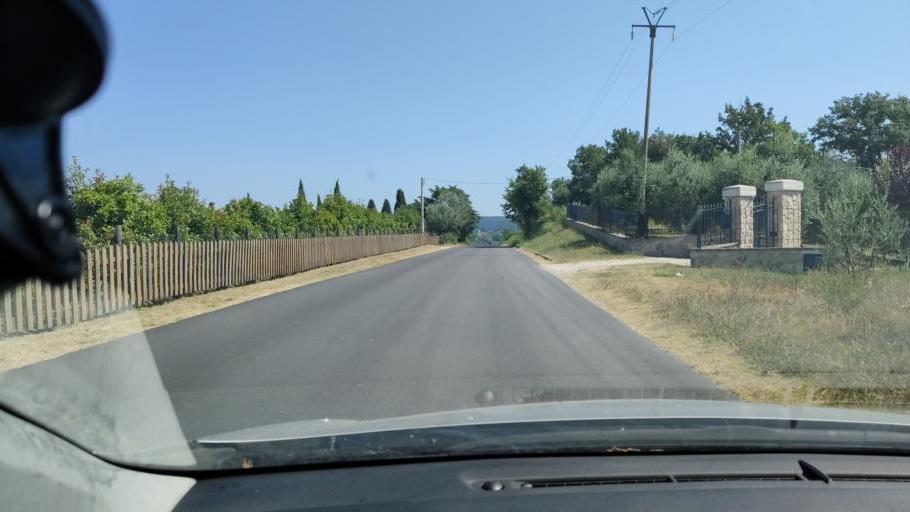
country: IT
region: Umbria
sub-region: Provincia di Terni
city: Fornole
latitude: 42.5212
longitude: 12.4331
